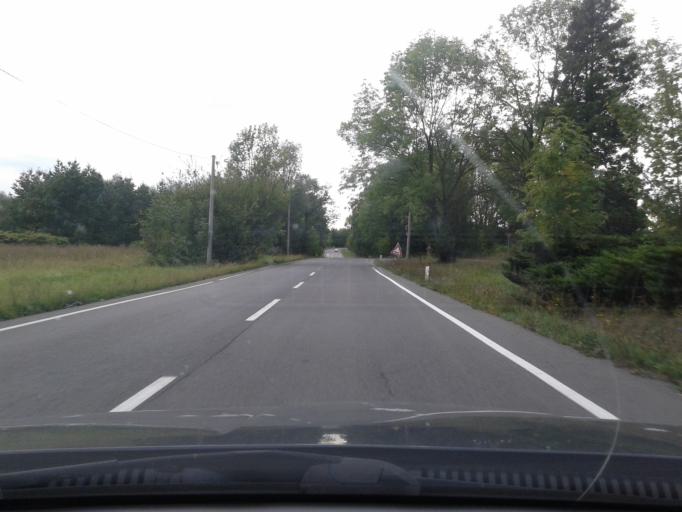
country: CZ
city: Doubrava
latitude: 49.8515
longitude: 18.4717
